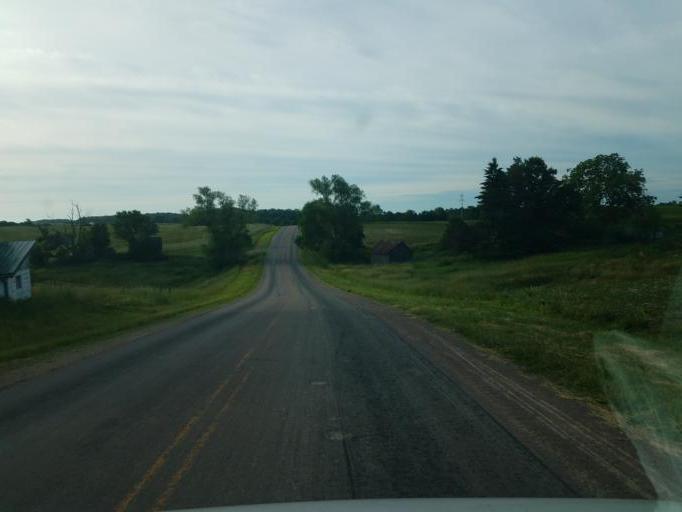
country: US
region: Wisconsin
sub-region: Vernon County
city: Hillsboro
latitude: 43.5985
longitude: -90.4168
